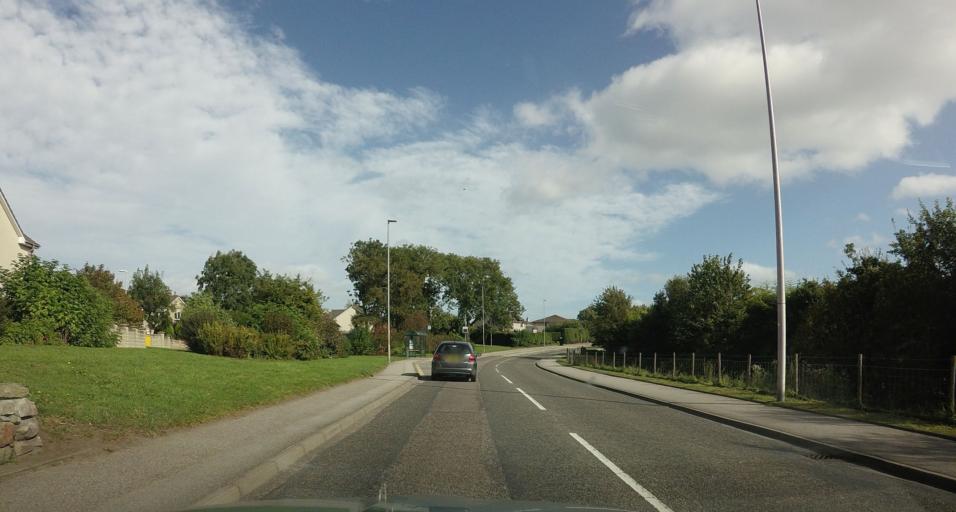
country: GB
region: Scotland
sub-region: Aberdeenshire
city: Westhill
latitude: 57.1521
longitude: -2.3075
